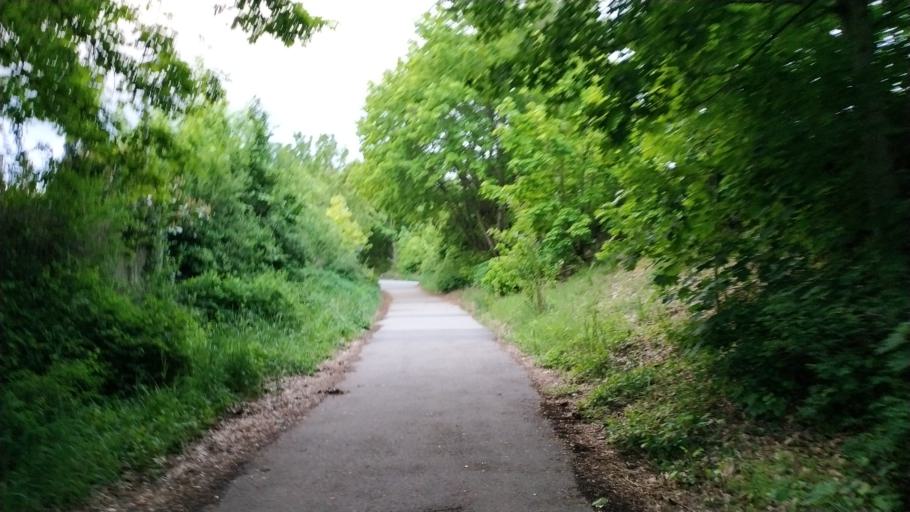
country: DE
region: Bavaria
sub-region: Regierungsbezirk Mittelfranken
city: Grossreuth bei Schweinau
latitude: 49.4268
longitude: 11.0544
